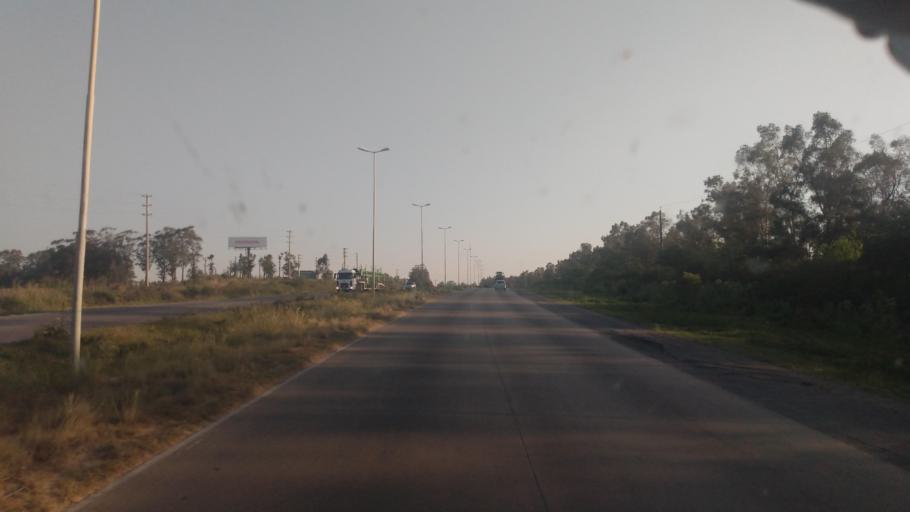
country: AR
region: Buenos Aires
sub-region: Partido de Campana
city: Campana
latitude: -34.2168
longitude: -58.9585
